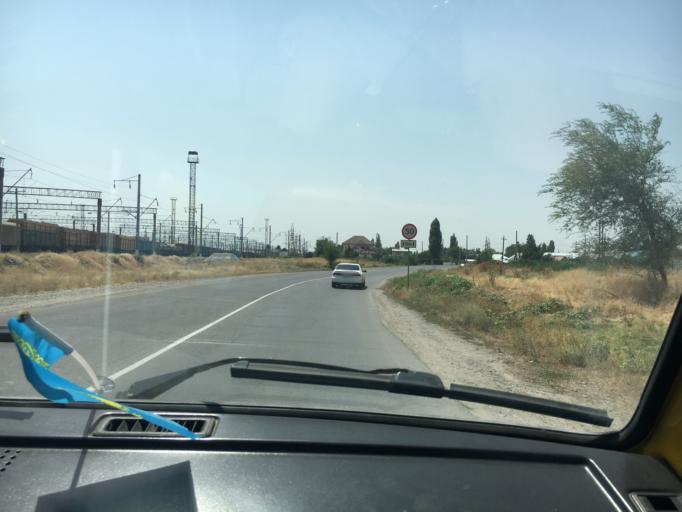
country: KZ
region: Zhambyl
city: Taraz
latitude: 42.8600
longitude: 71.3568
